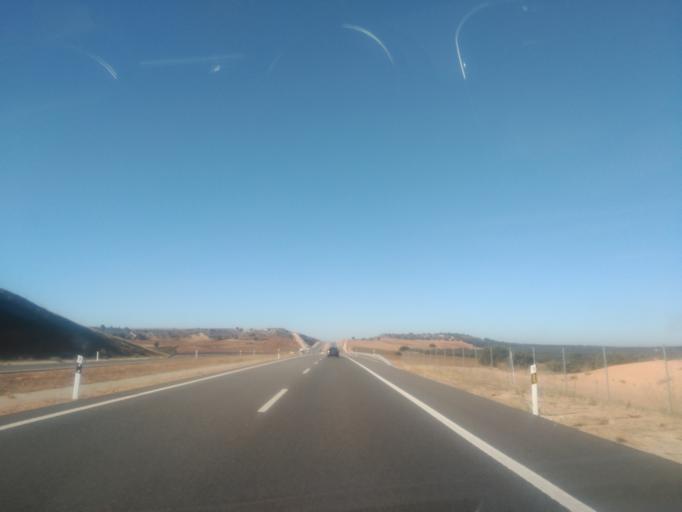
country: ES
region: Castille and Leon
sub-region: Provincia de Burgos
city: Campillo de Aranda
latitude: 41.6342
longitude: -3.7319
